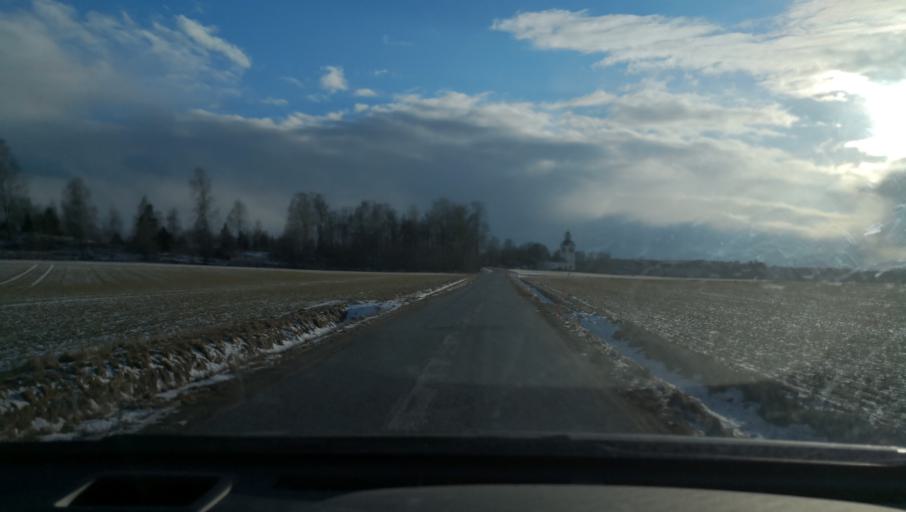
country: SE
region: Uppsala
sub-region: Enkopings Kommun
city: Irsta
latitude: 59.6857
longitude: 16.8552
